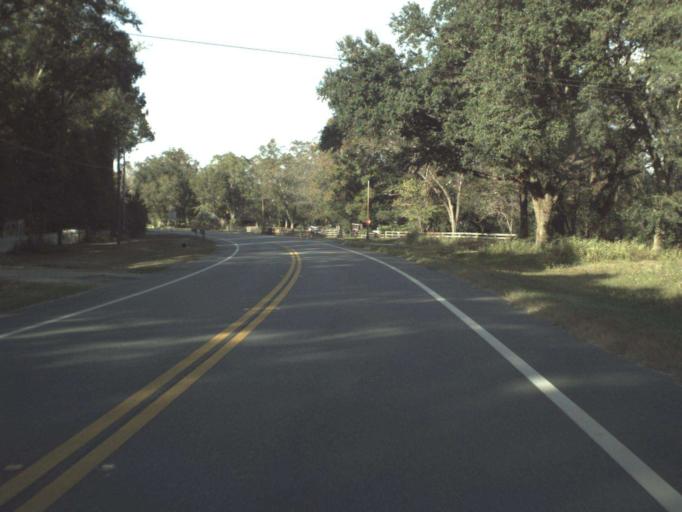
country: US
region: Florida
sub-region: Washington County
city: Chipley
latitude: 30.7670
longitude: -85.5673
